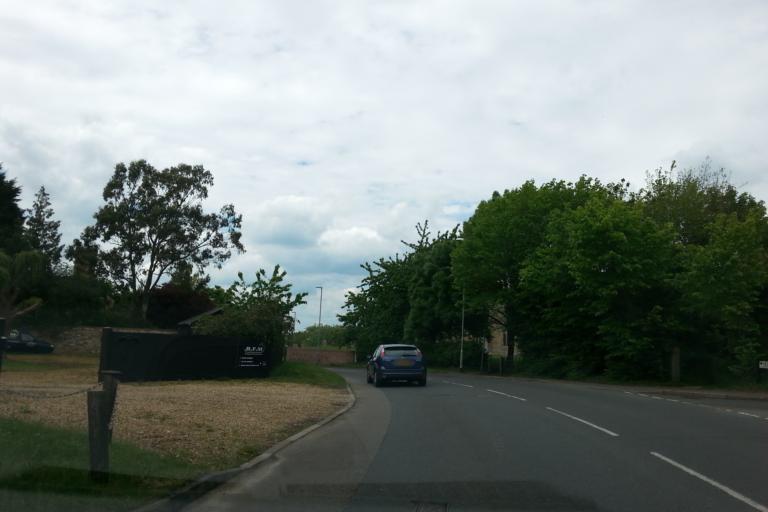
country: GB
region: England
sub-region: Cambridgeshire
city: Ramsey
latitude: 52.4362
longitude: -0.1070
